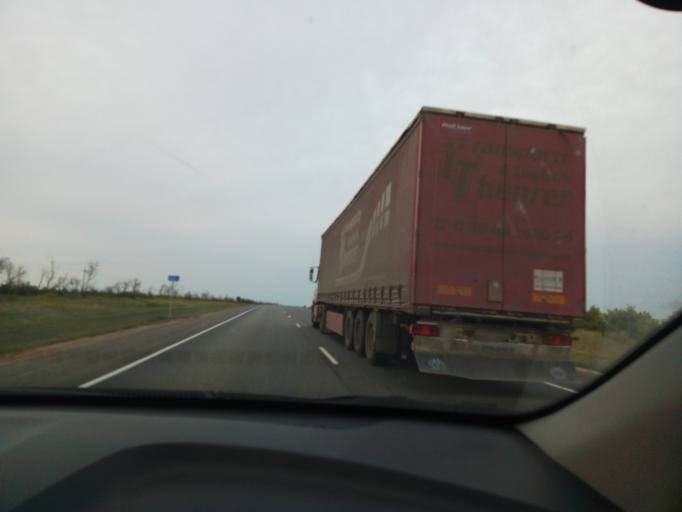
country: RU
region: Volgograd
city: Dubovka
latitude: 49.1524
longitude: 44.8387
